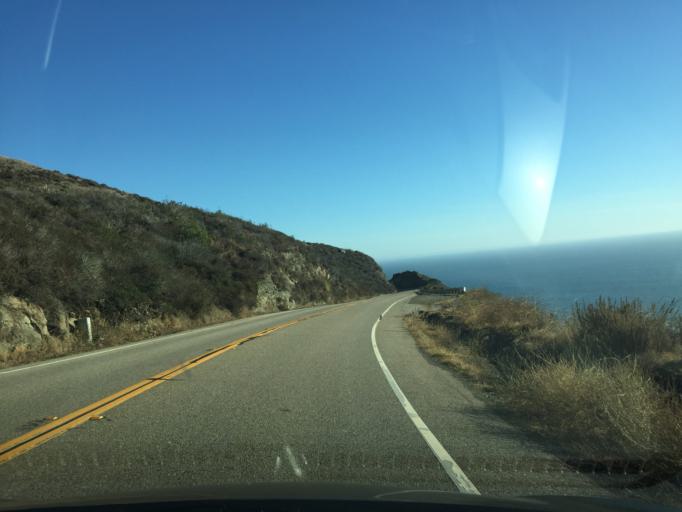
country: US
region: California
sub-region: San Luis Obispo County
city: Cambria
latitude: 35.8166
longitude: -121.3702
